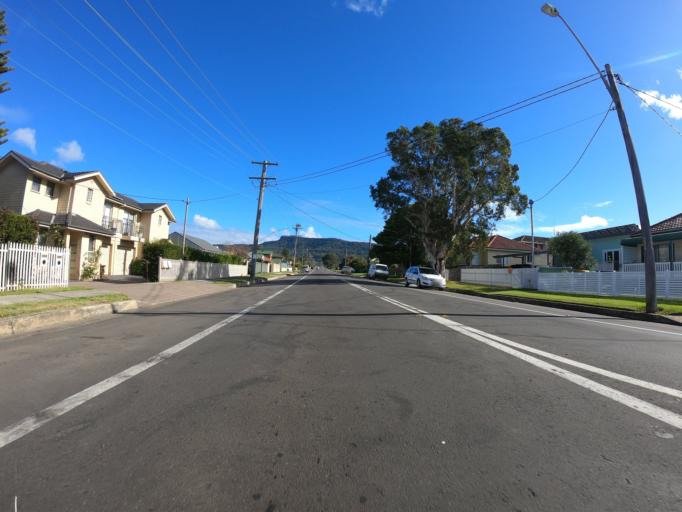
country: AU
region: New South Wales
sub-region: Wollongong
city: East Corrimal
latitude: -34.3689
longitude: 150.9161
